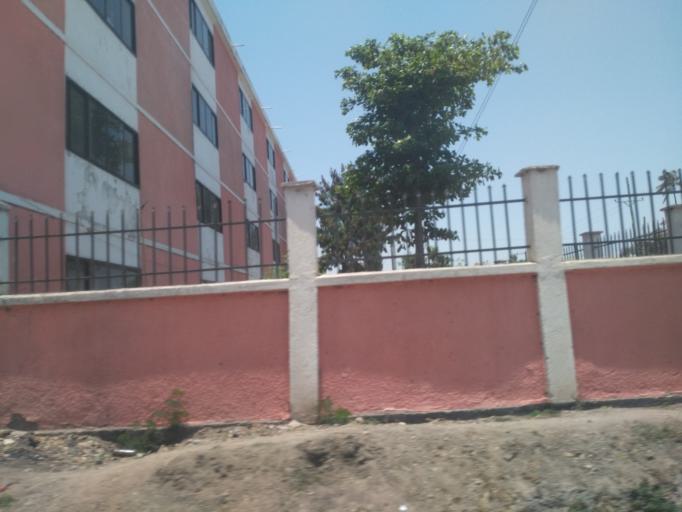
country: TZ
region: Dodoma
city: Dodoma
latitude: -6.1740
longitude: 35.7491
